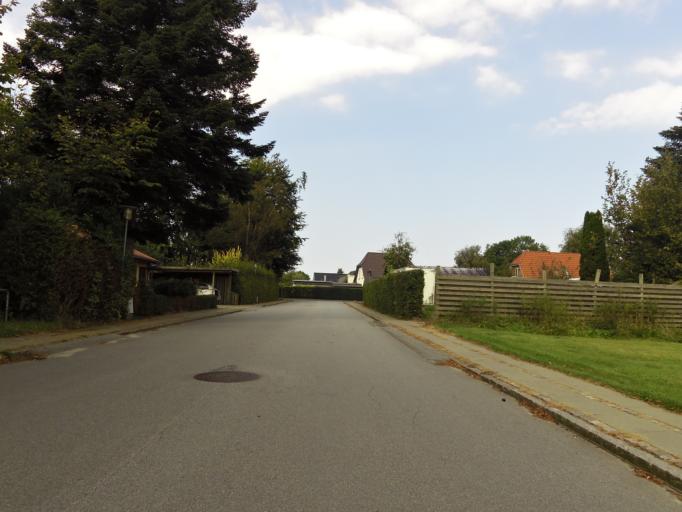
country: DK
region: South Denmark
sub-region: Vejen Kommune
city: Vejen
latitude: 55.4707
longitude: 9.1330
